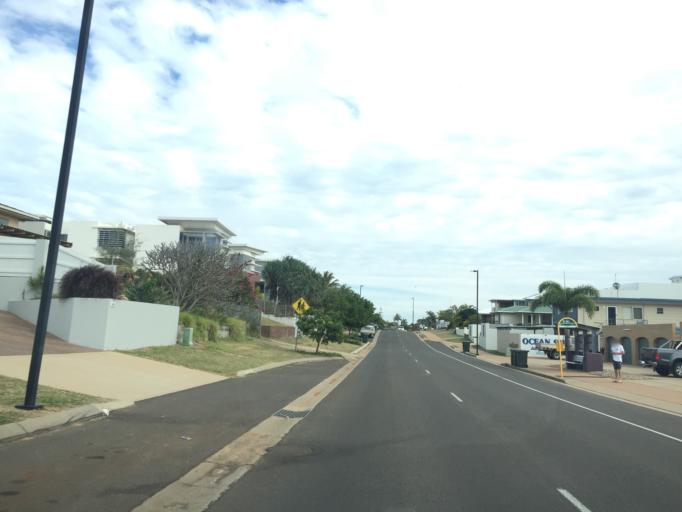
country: AU
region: Queensland
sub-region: Bundaberg
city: Bundaberg
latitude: -24.8224
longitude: 152.4652
